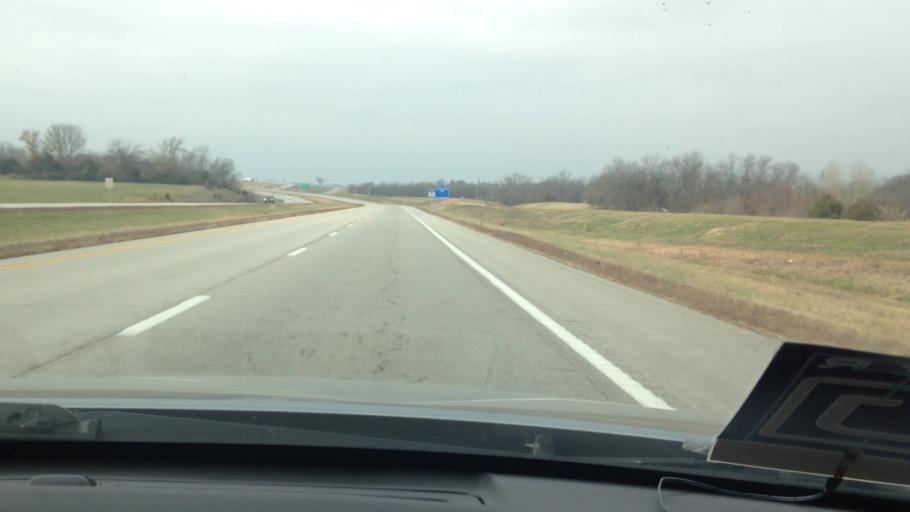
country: US
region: Missouri
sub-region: Cass County
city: Garden City
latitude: 38.5641
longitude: -94.1845
